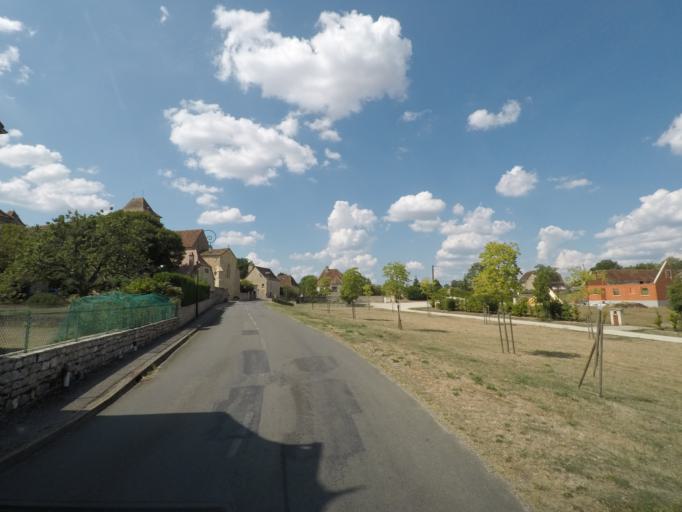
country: FR
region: Midi-Pyrenees
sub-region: Departement du Lot
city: Le Vigan
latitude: 44.6323
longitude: 1.5959
